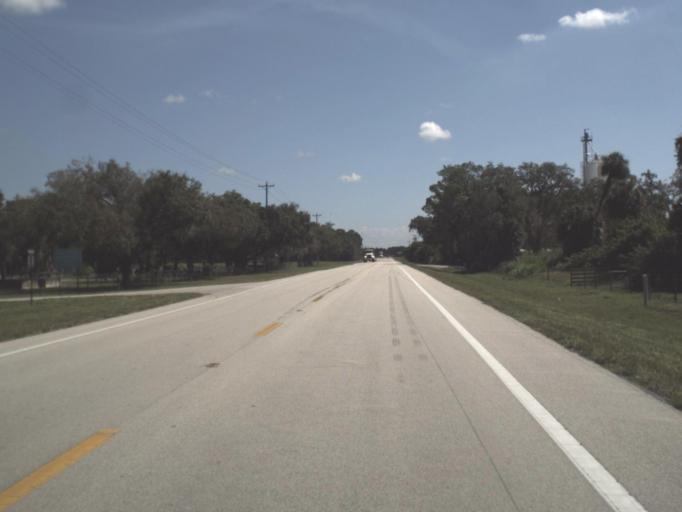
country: US
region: Florida
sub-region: Hendry County
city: Port LaBelle
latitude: 26.8159
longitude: -81.3024
